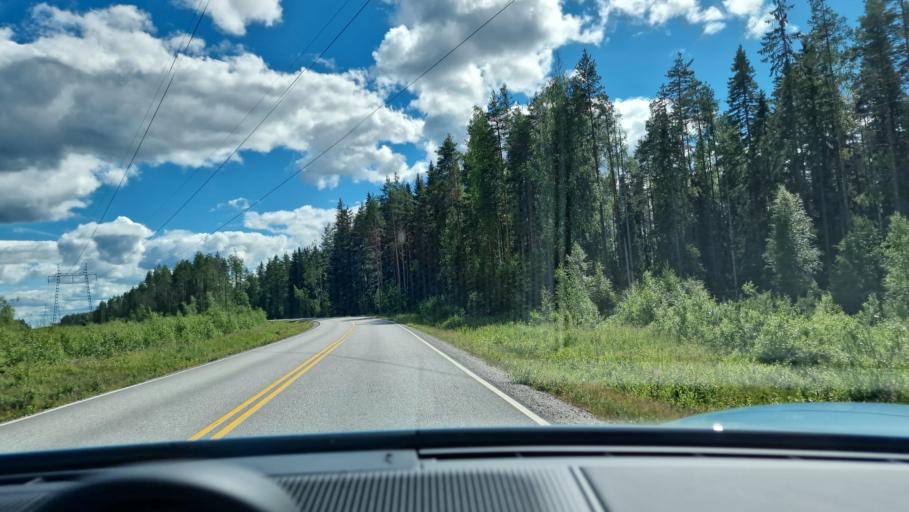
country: FI
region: Central Finland
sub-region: Saarijaervi-Viitasaari
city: Pylkoenmaeki
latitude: 62.6487
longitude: 24.5725
